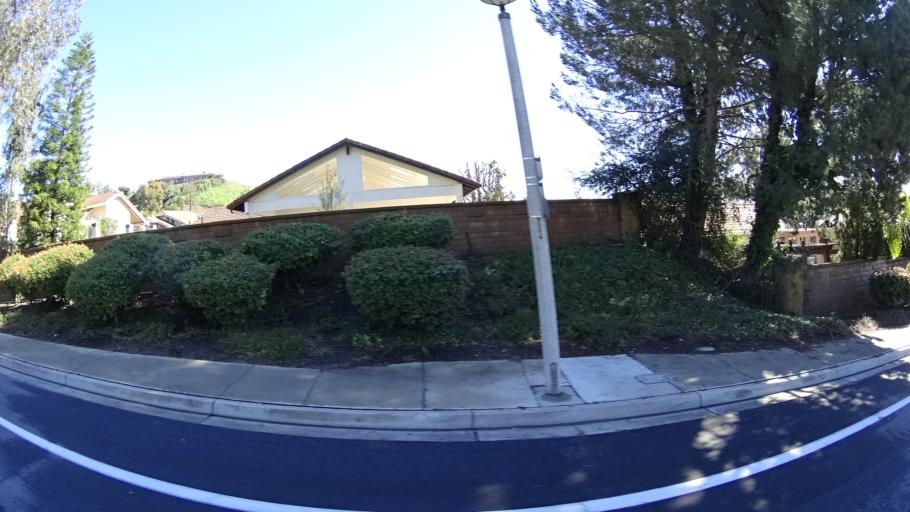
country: US
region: California
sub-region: Orange County
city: Yorba Linda
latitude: 33.8824
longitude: -117.7450
